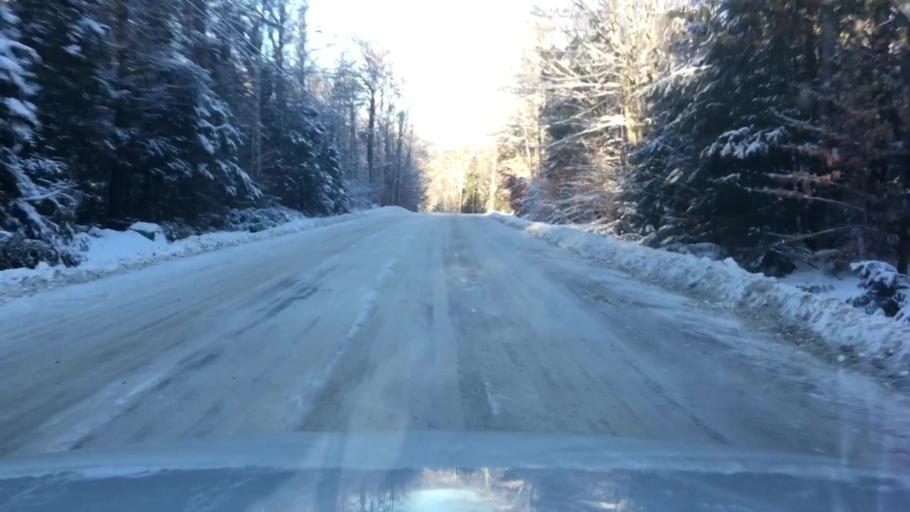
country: US
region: Maine
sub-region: Kennebec County
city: Belgrade
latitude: 44.4259
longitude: -69.8921
